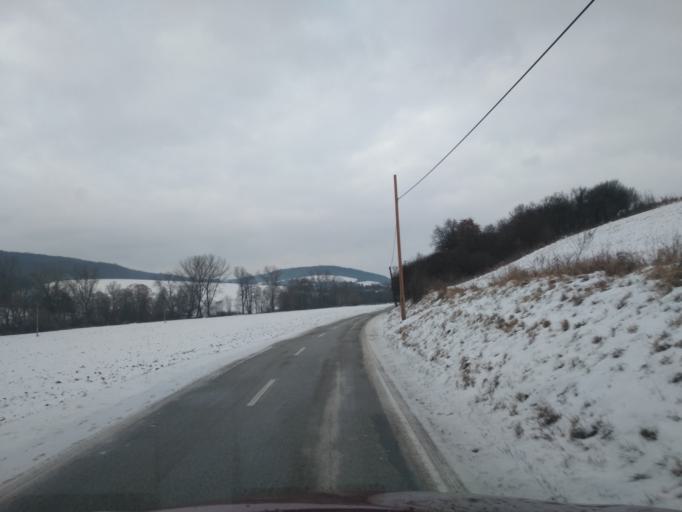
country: SK
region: Presovsky
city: Sabinov
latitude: 49.0274
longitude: 21.1042
